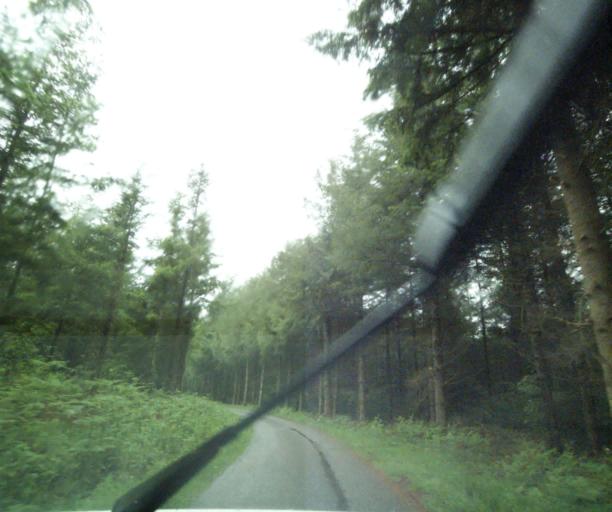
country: FR
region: Bourgogne
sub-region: Departement de Saone-et-Loire
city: Charolles
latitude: 46.3729
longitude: 4.3649
